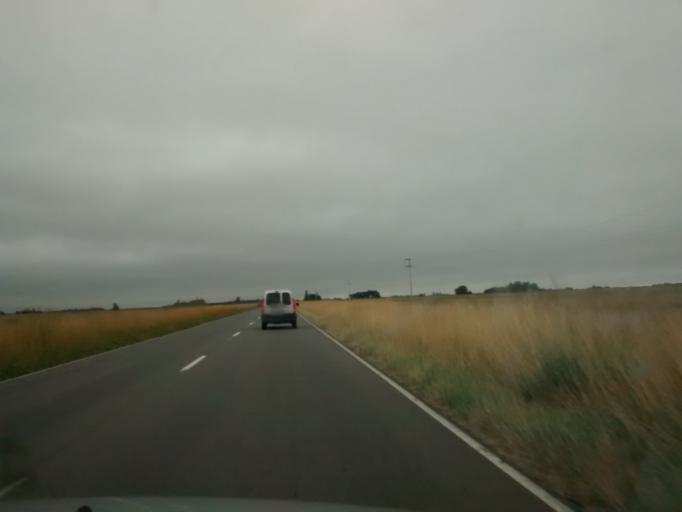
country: AR
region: Buenos Aires
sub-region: Partido de Ayacucho
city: Ayacucho
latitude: -37.0213
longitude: -58.5386
